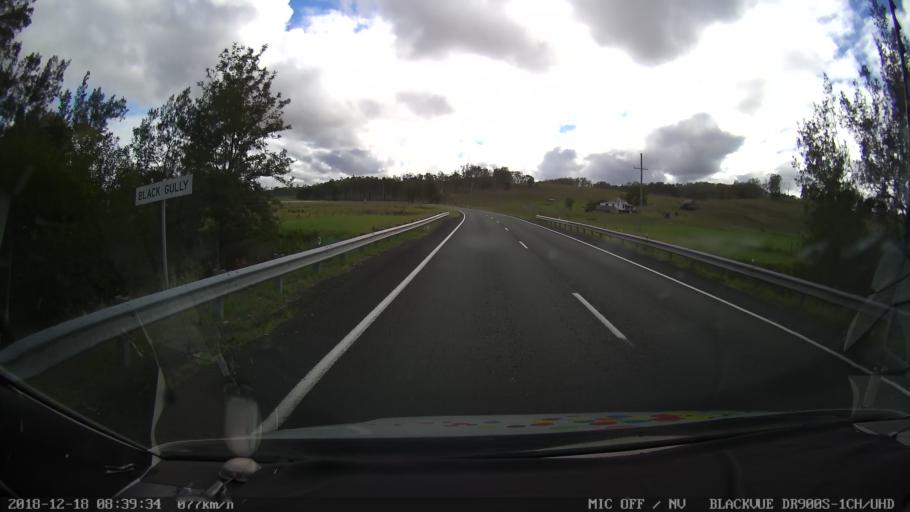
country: AU
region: New South Wales
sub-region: Kyogle
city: Kyogle
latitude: -28.2494
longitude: 152.8394
